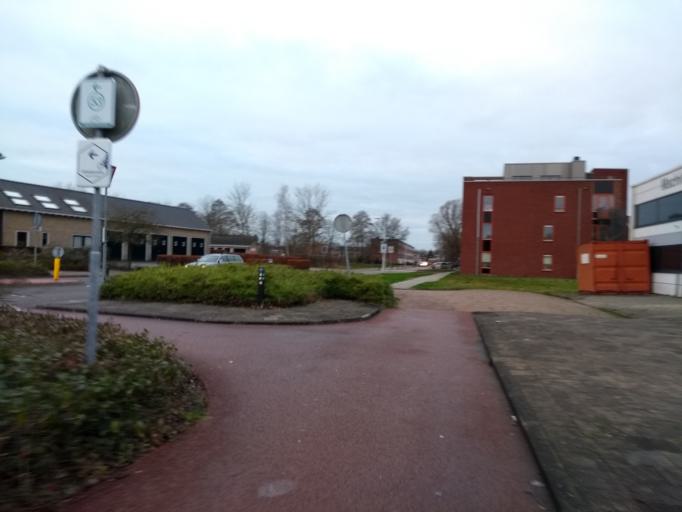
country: NL
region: Friesland
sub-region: Sudwest Fryslan
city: Sneek
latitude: 53.0271
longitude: 5.6561
